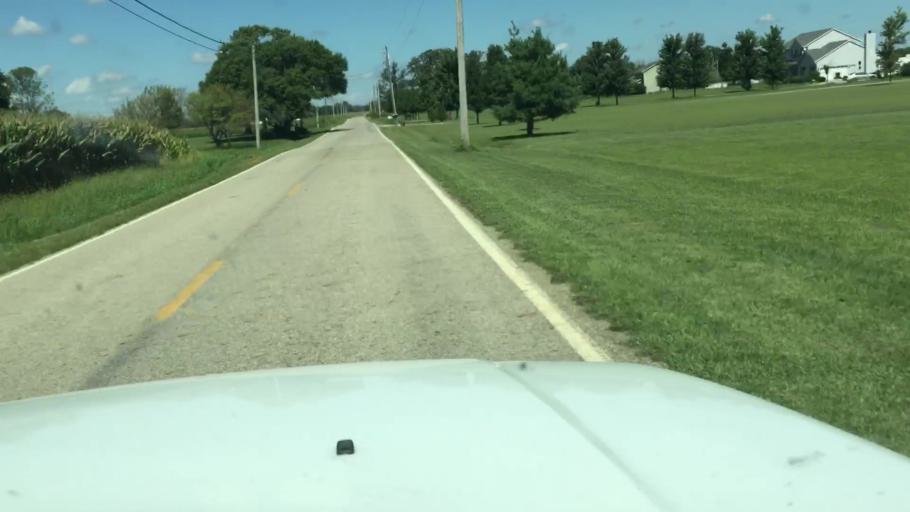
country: US
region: Ohio
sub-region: Madison County
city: Mount Sterling
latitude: 39.6710
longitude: -83.2353
